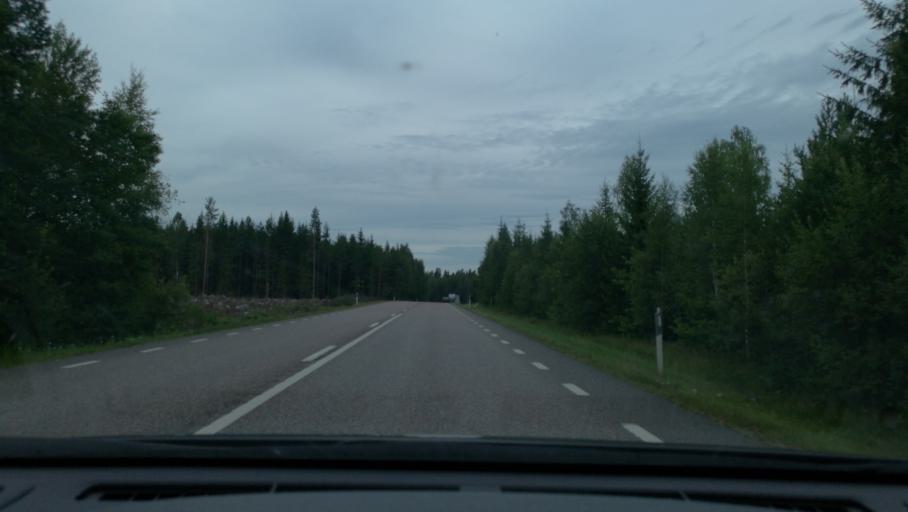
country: SE
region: Soedermanland
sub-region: Katrineholms Kommun
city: Katrineholm
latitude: 59.0297
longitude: 16.2141
